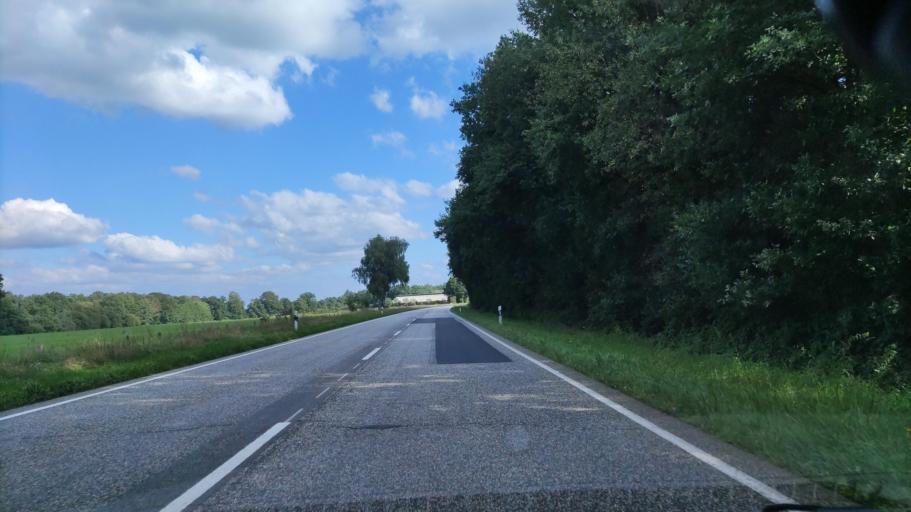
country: DE
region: Schleswig-Holstein
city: Jevenstedt
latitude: 54.2235
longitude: 9.7057
